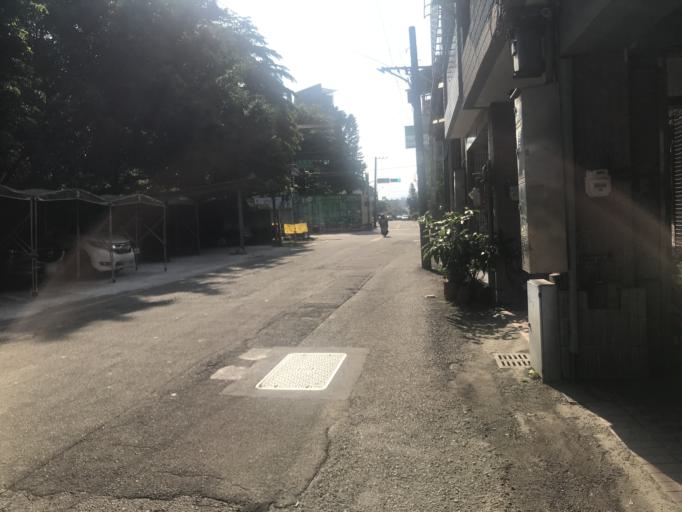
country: TW
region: Taiwan
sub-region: Taichung City
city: Taichung
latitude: 24.1109
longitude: 120.6573
